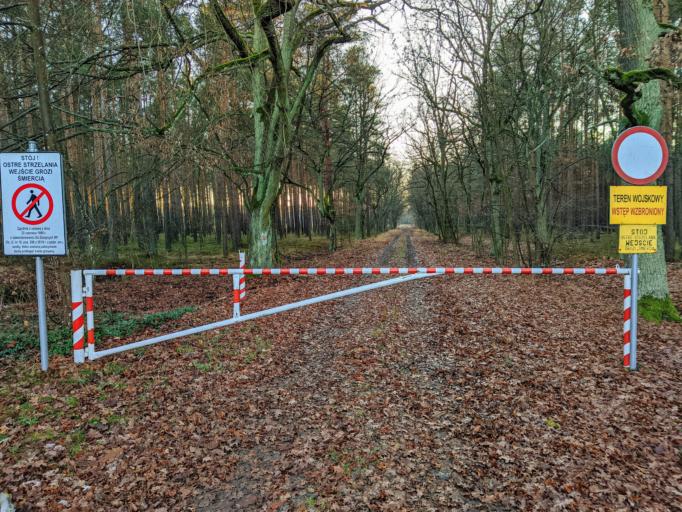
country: PL
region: Lubusz
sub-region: Powiat zaganski
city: Zagan
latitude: 51.5854
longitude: 15.3054
